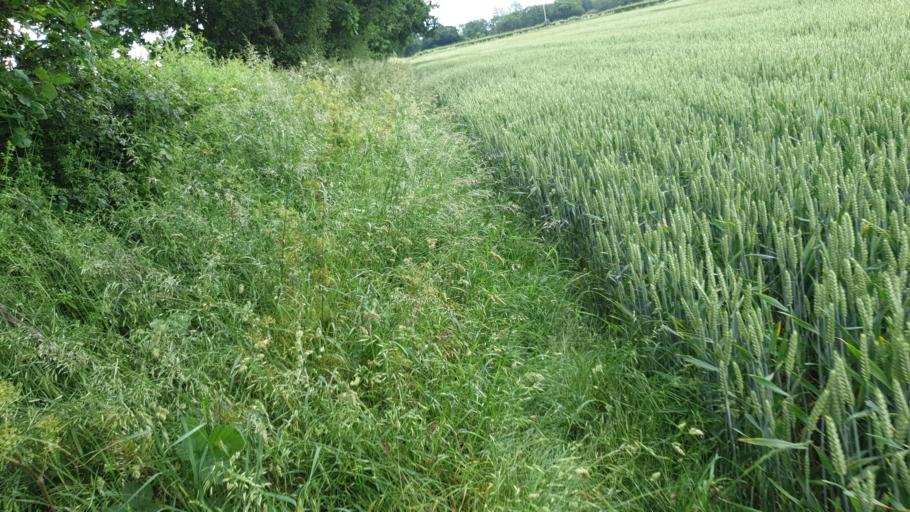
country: GB
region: England
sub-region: Essex
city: Great Bentley
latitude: 51.8814
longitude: 1.1129
